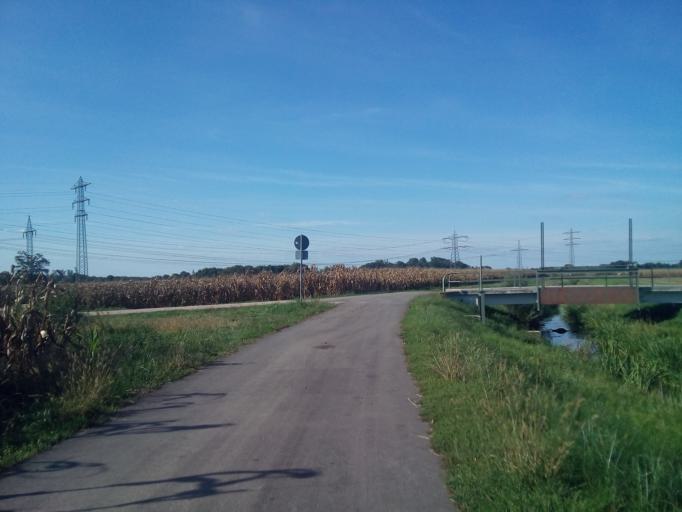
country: DE
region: Baden-Wuerttemberg
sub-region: Karlsruhe Region
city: Zell
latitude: 48.6716
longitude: 8.0717
